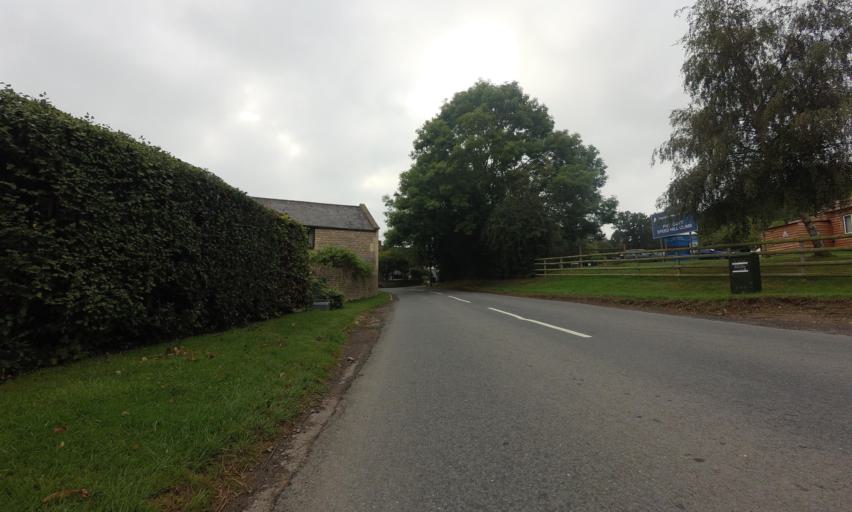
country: GB
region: England
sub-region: Gloucestershire
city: Gotherington
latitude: 51.9662
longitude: -2.0225
